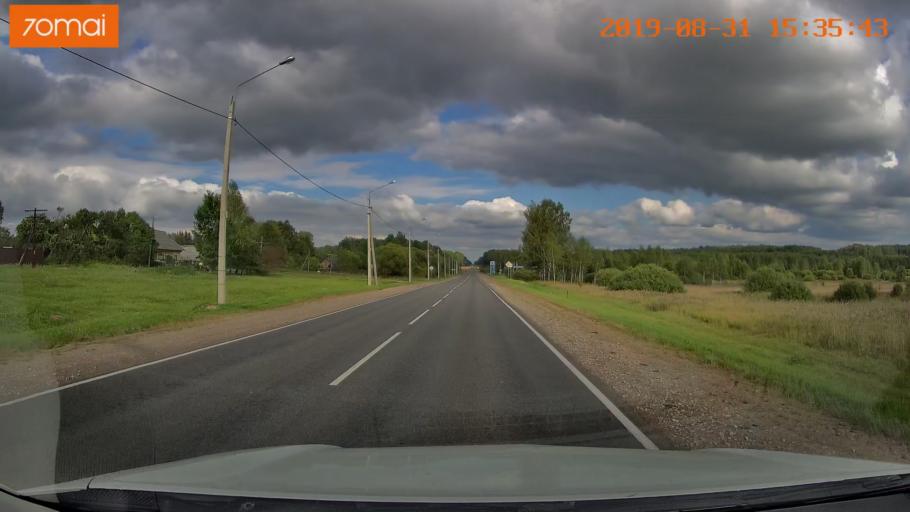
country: RU
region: Kaluga
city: Mosal'sk
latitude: 54.6069
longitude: 34.7432
